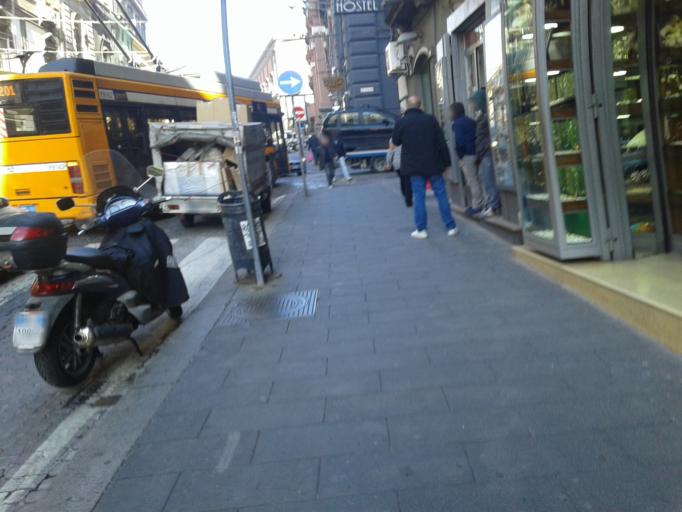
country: IT
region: Campania
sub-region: Provincia di Napoli
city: Napoli
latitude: 40.8516
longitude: 14.2501
